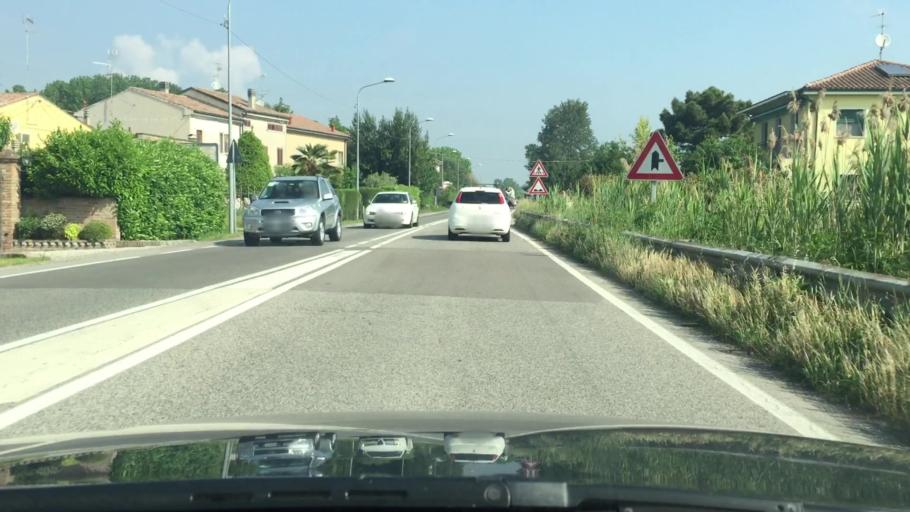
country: IT
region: Emilia-Romagna
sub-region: Provincia di Ferrara
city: Pontegradella
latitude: 44.8077
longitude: 11.6357
